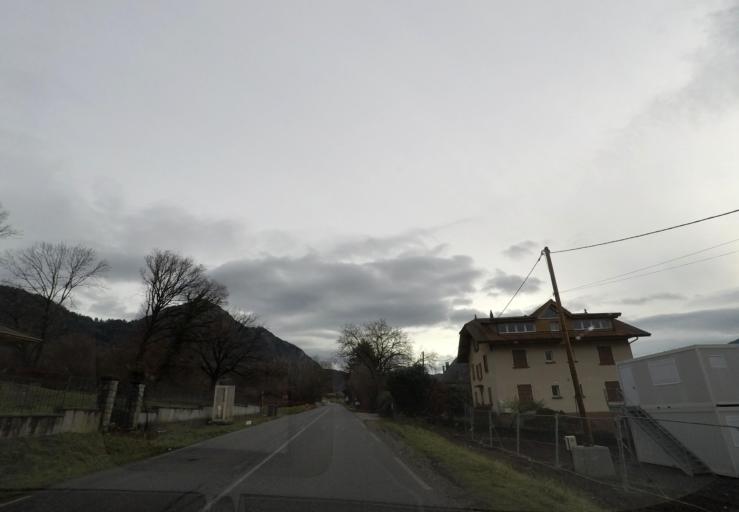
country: FR
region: Rhone-Alpes
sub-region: Departement de la Haute-Savoie
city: Marignier
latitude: 46.0909
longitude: 6.5137
